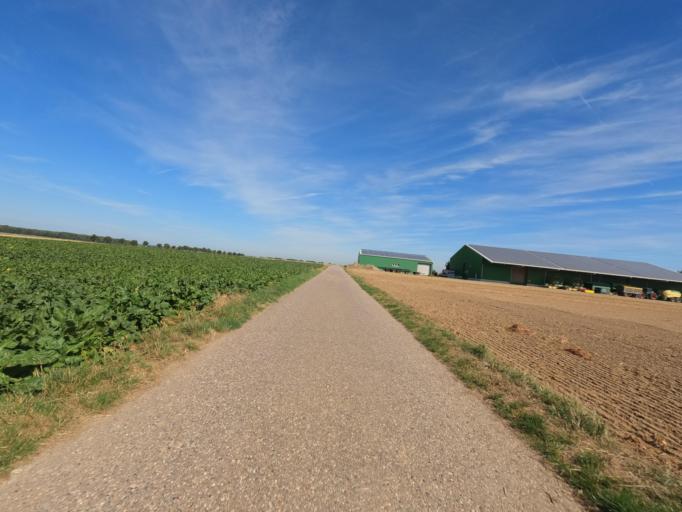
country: DE
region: North Rhine-Westphalia
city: Erkelenz
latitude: 51.0375
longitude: 6.3546
